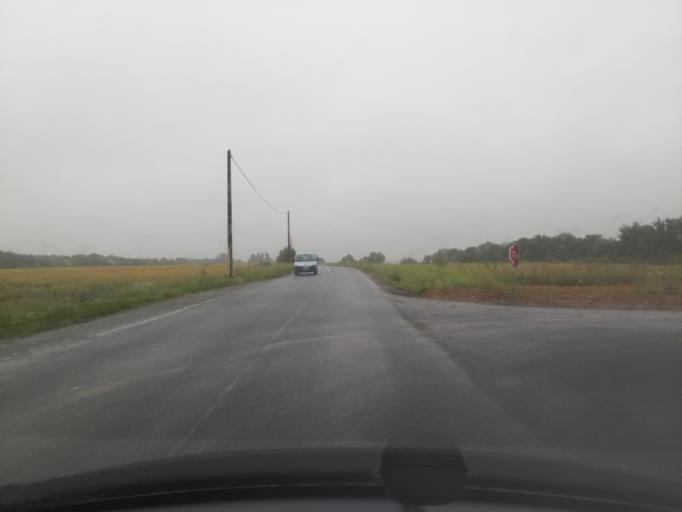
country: FR
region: Poitou-Charentes
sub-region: Departement de la Charente-Maritime
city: Saint-Jean-de-Liversay
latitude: 46.2389
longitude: -0.8814
